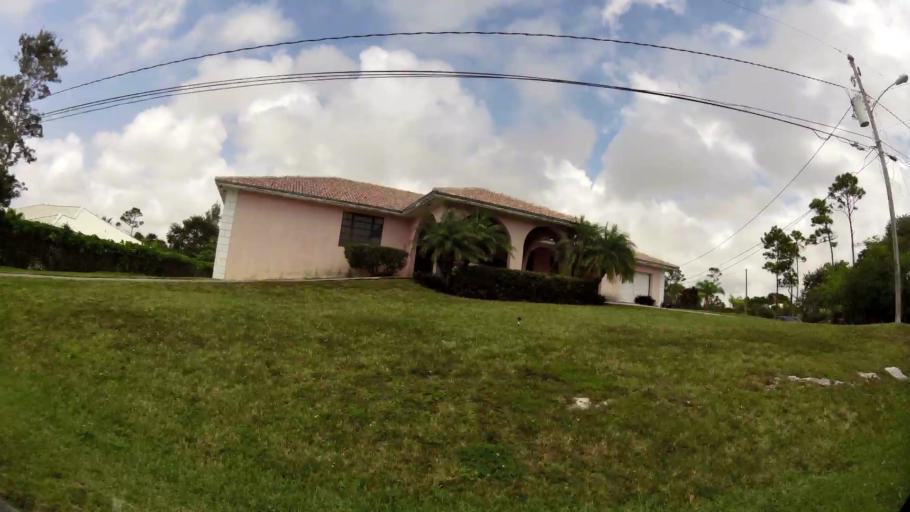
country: BS
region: Freeport
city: Lucaya
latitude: 26.5211
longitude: -78.6478
